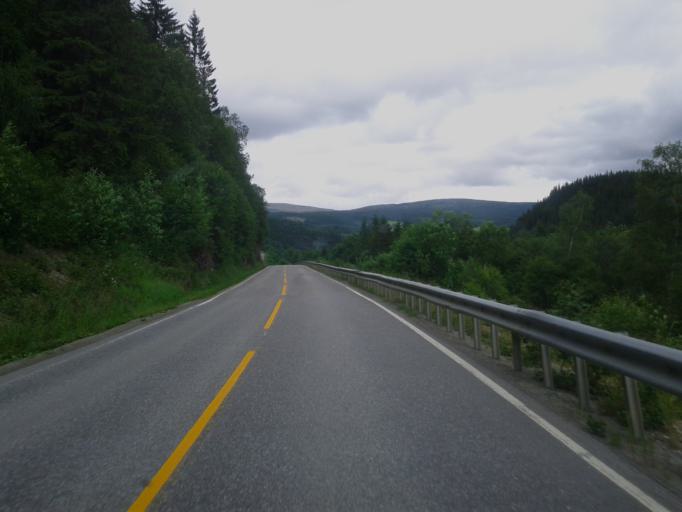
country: NO
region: Sor-Trondelag
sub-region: Klaebu
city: Klaebu
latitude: 62.9447
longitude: 10.6771
